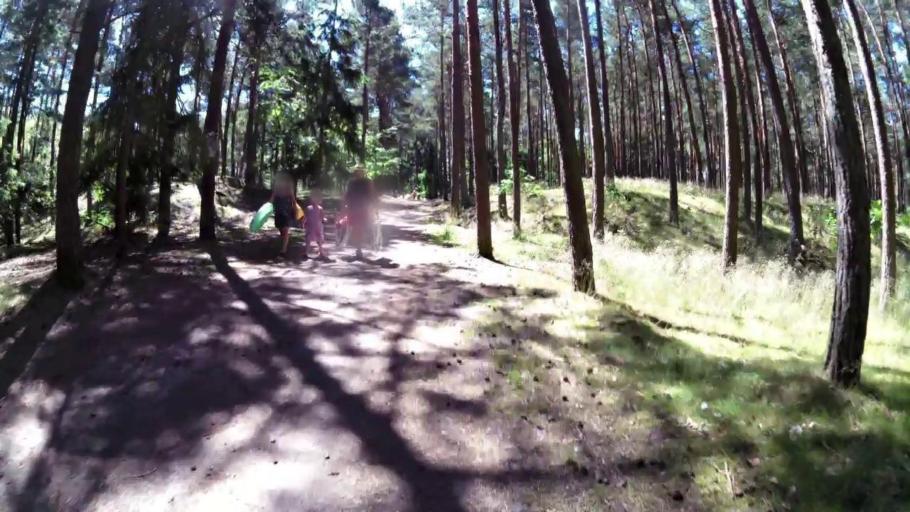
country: PL
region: West Pomeranian Voivodeship
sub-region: Powiat gryficki
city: Pobierowo
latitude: 54.0475
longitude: 14.8727
